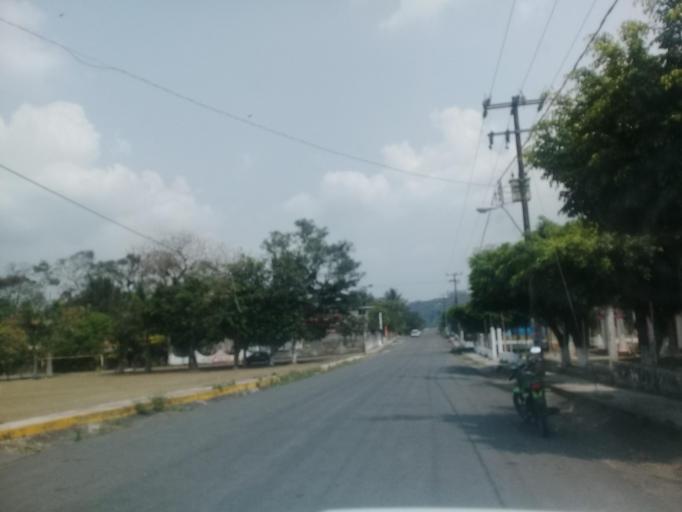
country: MX
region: Veracruz
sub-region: Cordoba
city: San Jose de Tapia
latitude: 18.8170
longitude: -96.9821
